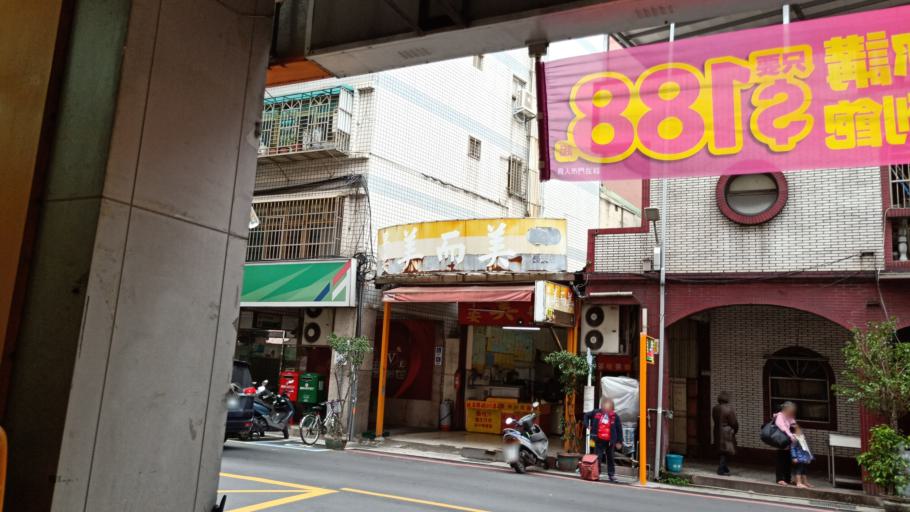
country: TW
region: Taipei
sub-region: Taipei
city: Banqiao
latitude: 25.0830
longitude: 121.4594
